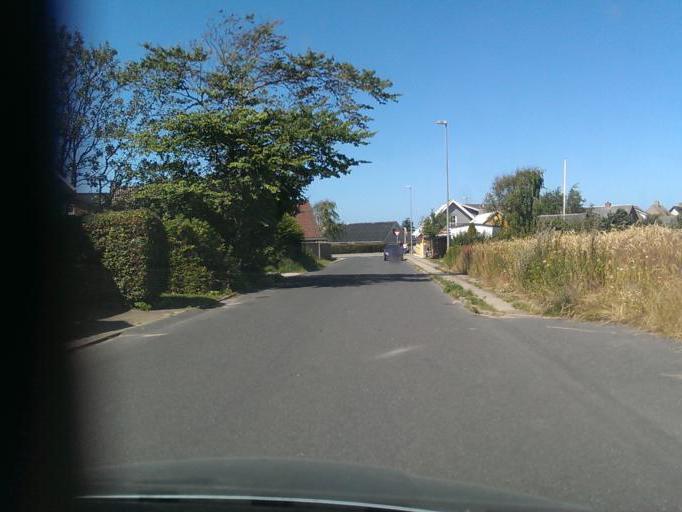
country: DK
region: North Denmark
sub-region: Jammerbugt Kommune
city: Pandrup
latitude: 57.3150
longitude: 9.7117
